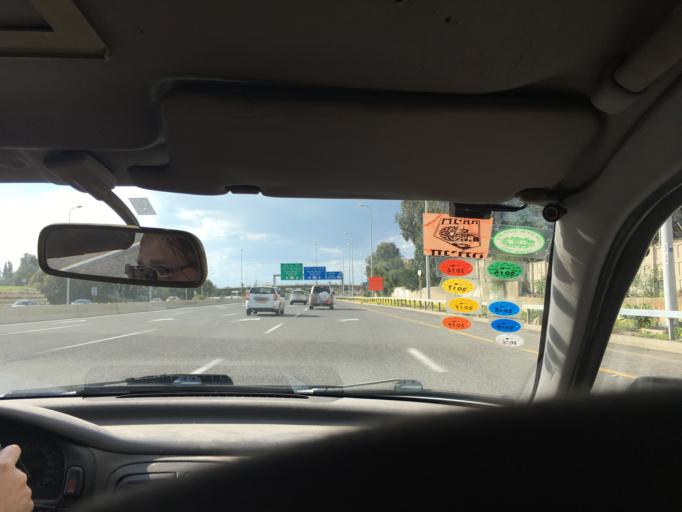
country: IL
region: Tel Aviv
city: Ramat HaSharon
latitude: 32.1389
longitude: 34.8178
